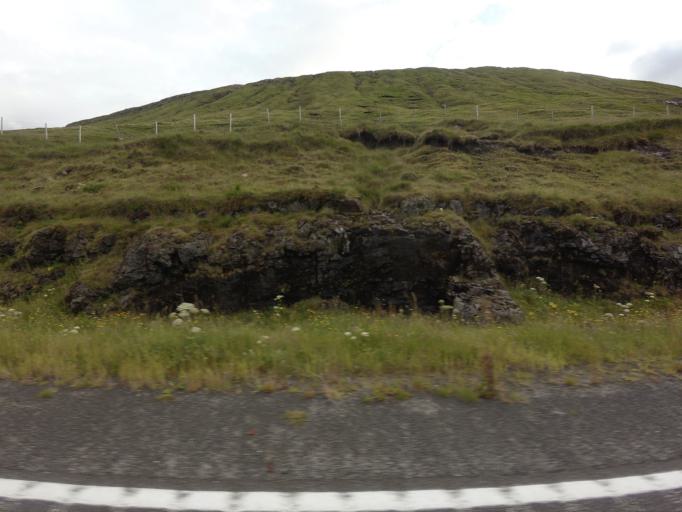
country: FO
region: Streymoy
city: Kollafjordhur
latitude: 62.1643
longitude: -6.9497
